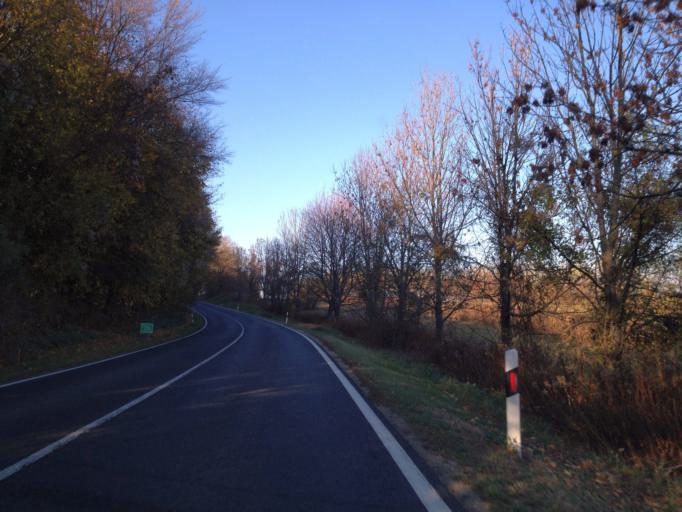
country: HU
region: Veszprem
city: Zirc
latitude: 47.3181
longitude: 17.8764
